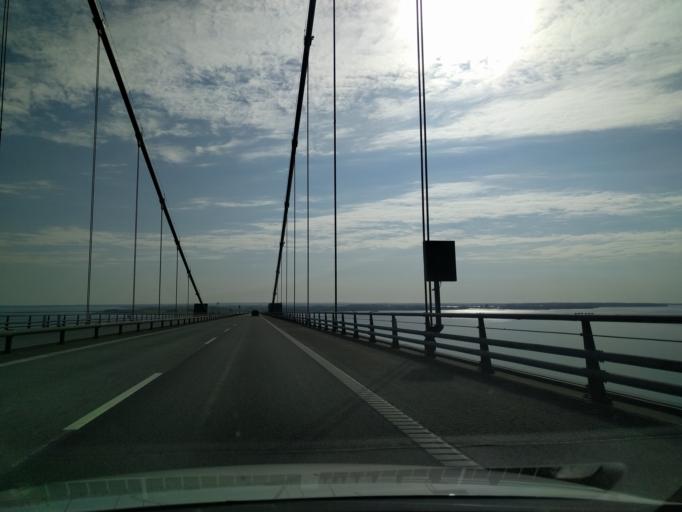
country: DK
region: Zealand
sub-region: Slagelse Kommune
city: Korsor
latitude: 55.3436
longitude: 11.0525
